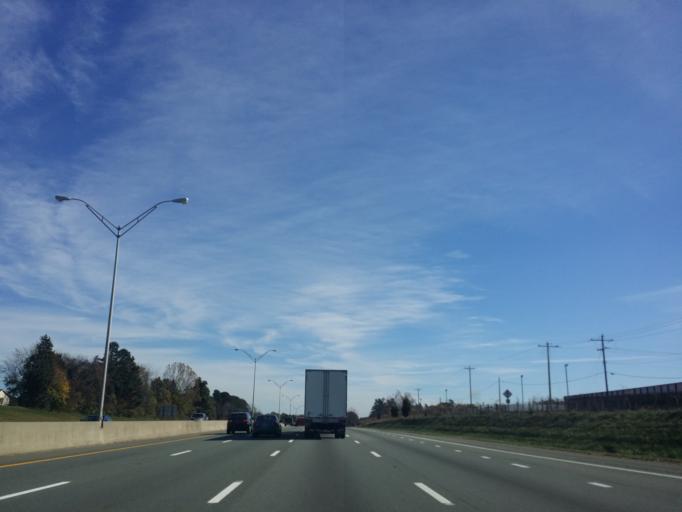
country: US
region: North Carolina
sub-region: Alamance County
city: Graham
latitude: 36.0630
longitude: -79.4243
